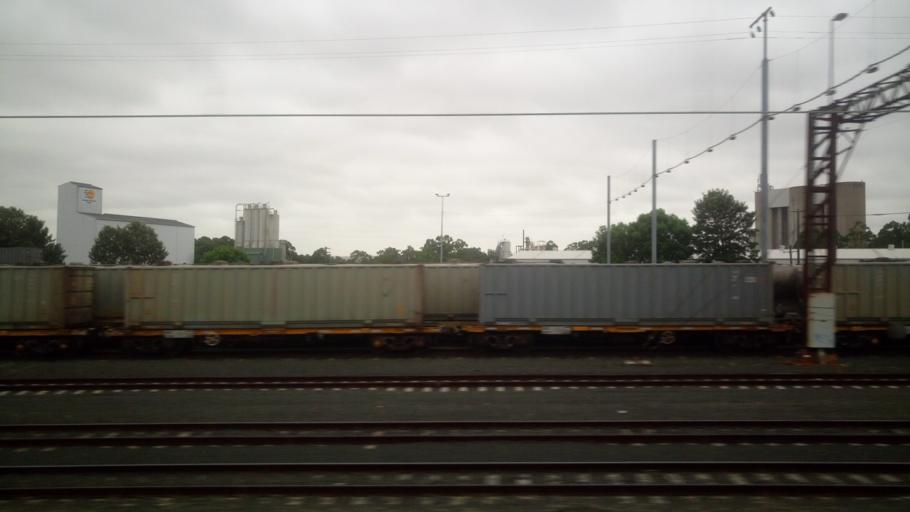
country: AU
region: New South Wales
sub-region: Parramatta
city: Granville
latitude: -33.8400
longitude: 151.0232
